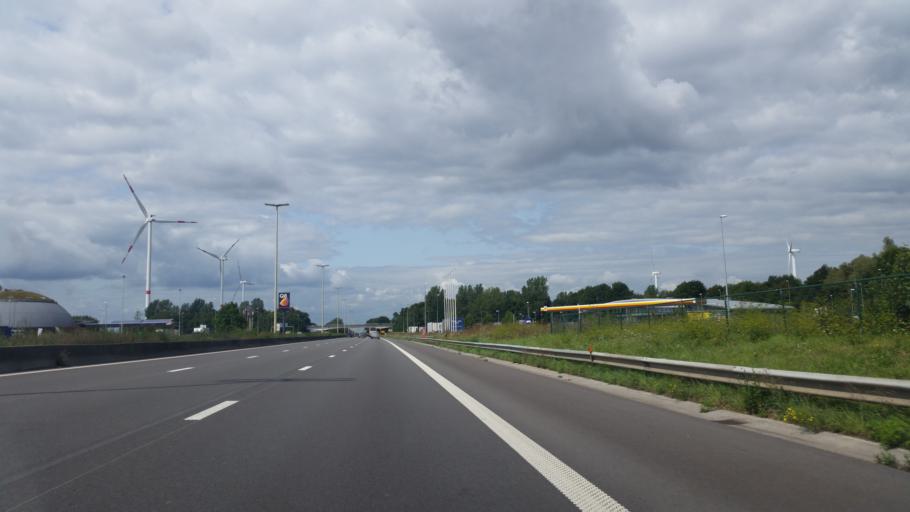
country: BE
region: Wallonia
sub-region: Province du Brabant Wallon
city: Perwez
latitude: 50.5984
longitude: 4.7931
